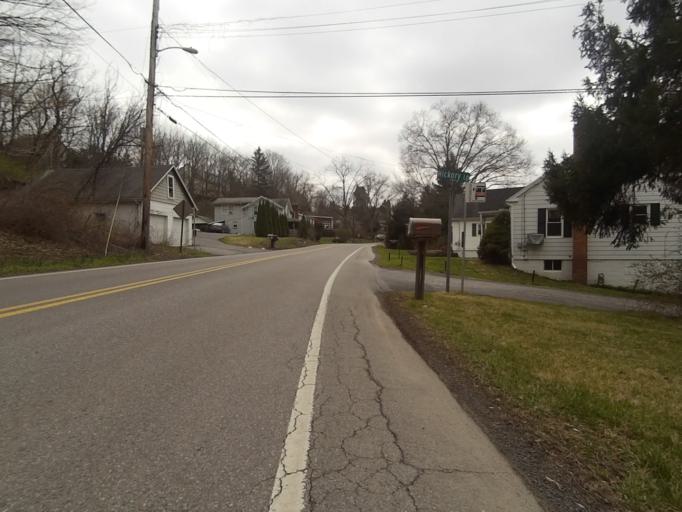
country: US
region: Pennsylvania
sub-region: Centre County
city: Lemont
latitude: 40.8152
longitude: -77.8189
